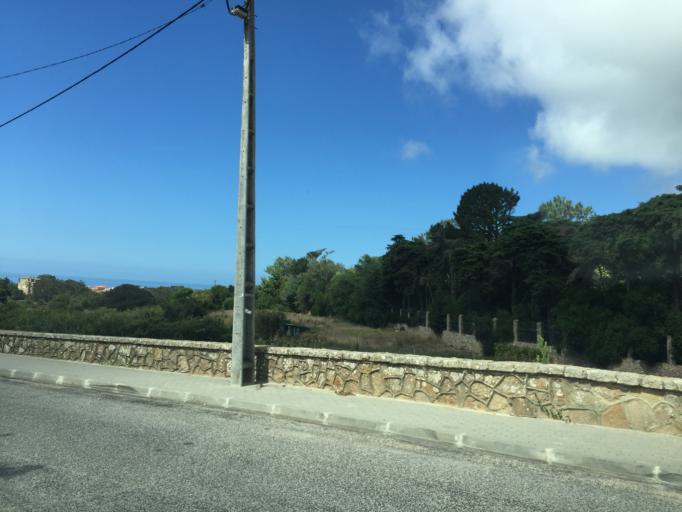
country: PT
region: Lisbon
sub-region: Sintra
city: Colares
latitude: 38.7592
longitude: -9.4451
